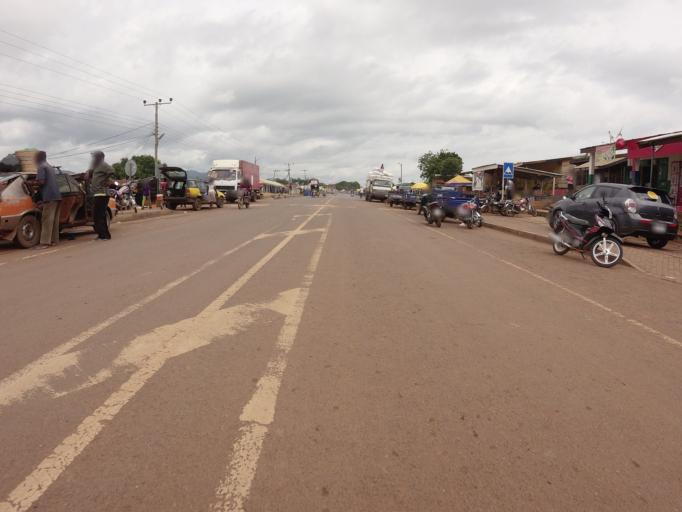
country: TG
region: Centrale
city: Sotouboua
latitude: 8.2624
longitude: 0.5212
